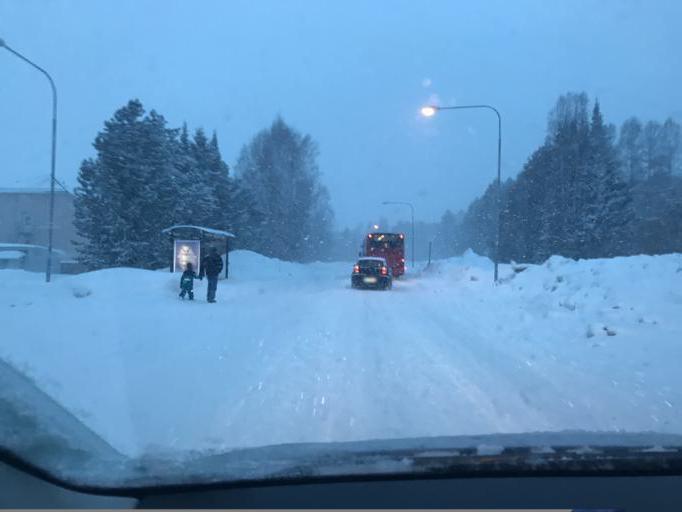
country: SE
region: Norrbotten
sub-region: Lulea Kommun
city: Lulea
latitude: 65.6195
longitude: 22.1291
